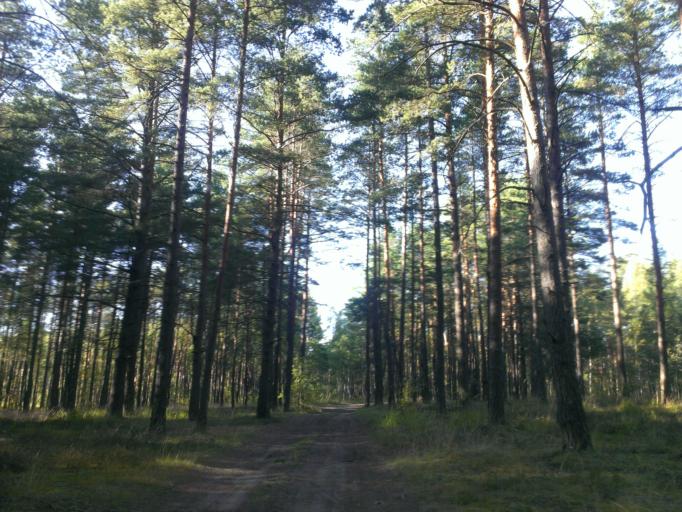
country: LV
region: Riga
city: Jaunciems
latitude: 57.0477
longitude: 24.2430
